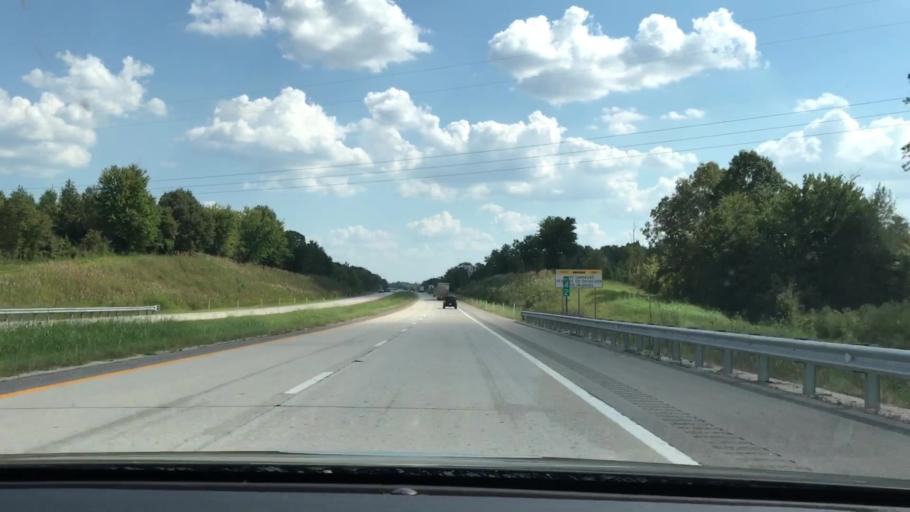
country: US
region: Kentucky
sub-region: Ohio County
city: Oak Grove
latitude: 37.3679
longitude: -86.7992
